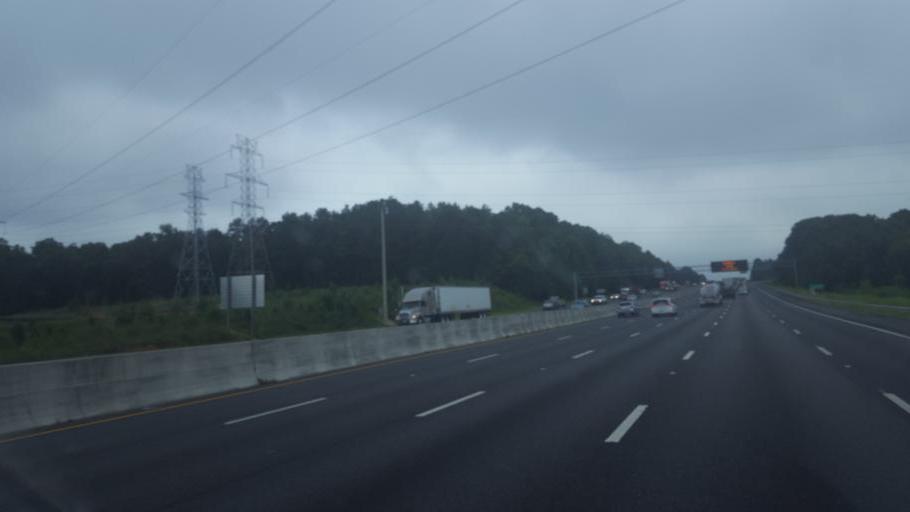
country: US
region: South Carolina
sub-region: York County
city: Fort Mill
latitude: 34.9910
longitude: -80.9808
